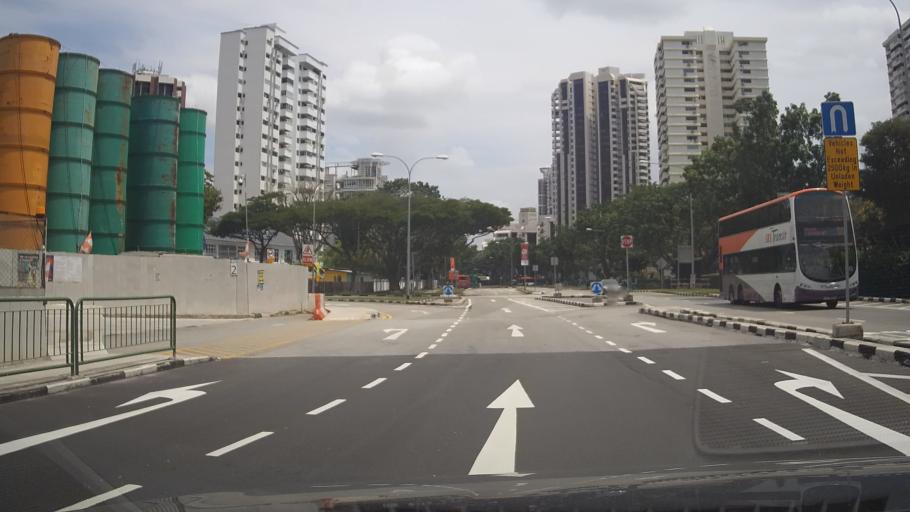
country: SG
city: Singapore
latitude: 1.3104
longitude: 103.9317
